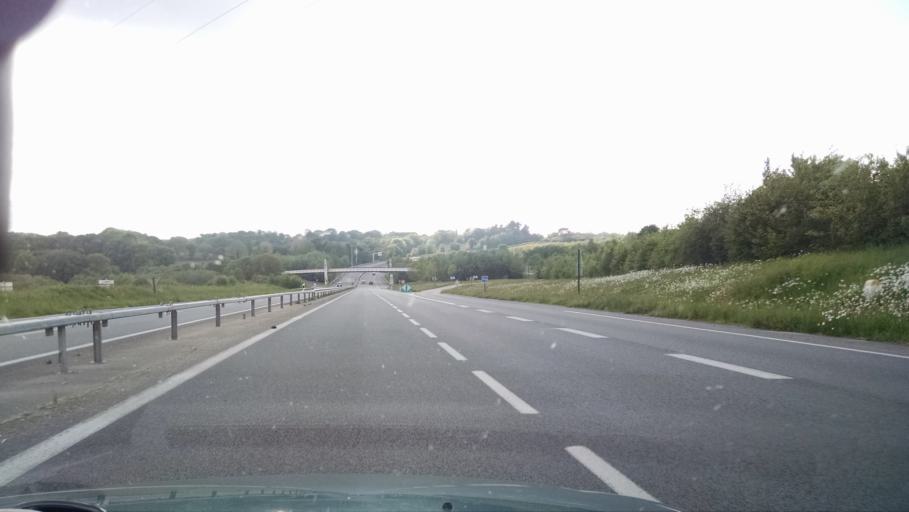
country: FR
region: Brittany
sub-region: Departement du Finistere
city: Morlaix
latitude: 48.5820
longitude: -3.8680
